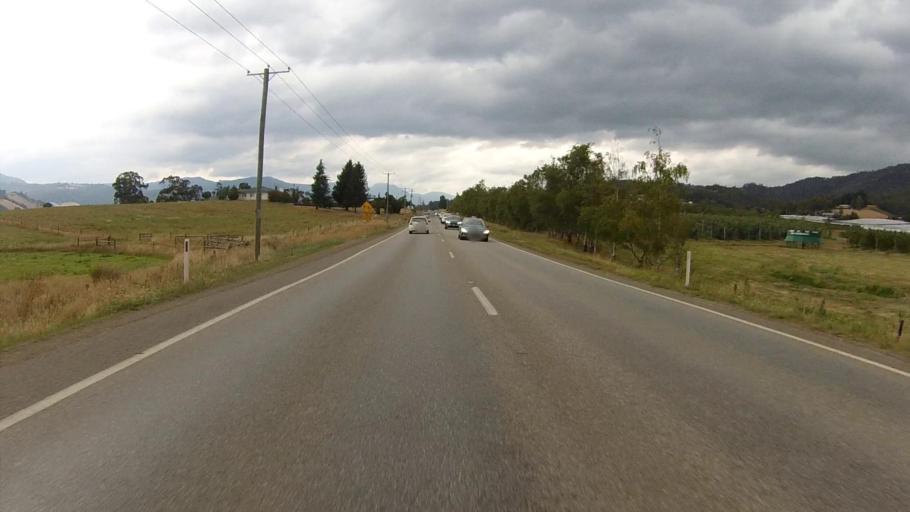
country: AU
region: Tasmania
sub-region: Huon Valley
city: Huonville
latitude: -43.0164
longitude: 147.0601
